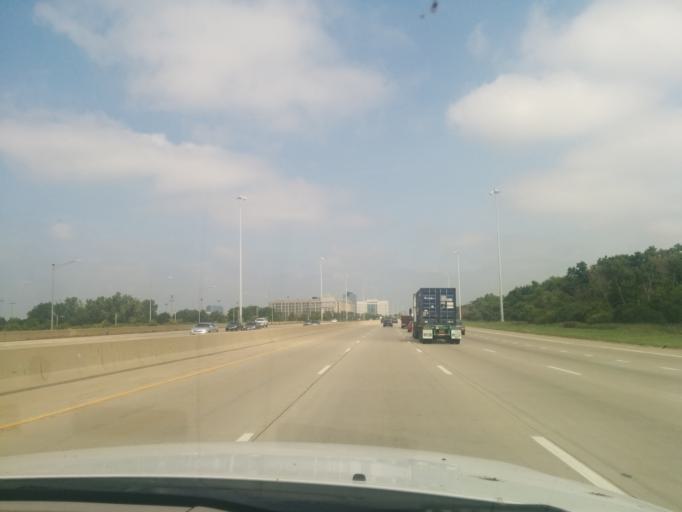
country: US
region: Illinois
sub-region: DuPage County
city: Itasca
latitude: 42.0184
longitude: -88.0309
